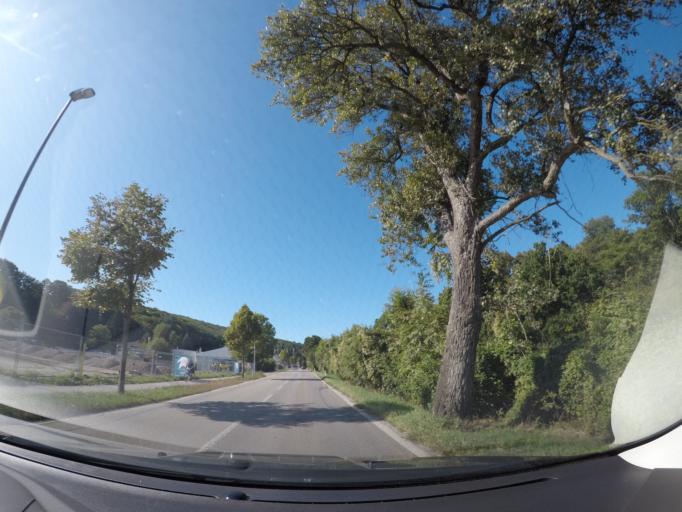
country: AT
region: Lower Austria
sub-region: Politischer Bezirk Modling
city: Kaltenleutgeben
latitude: 48.1415
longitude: 16.1992
